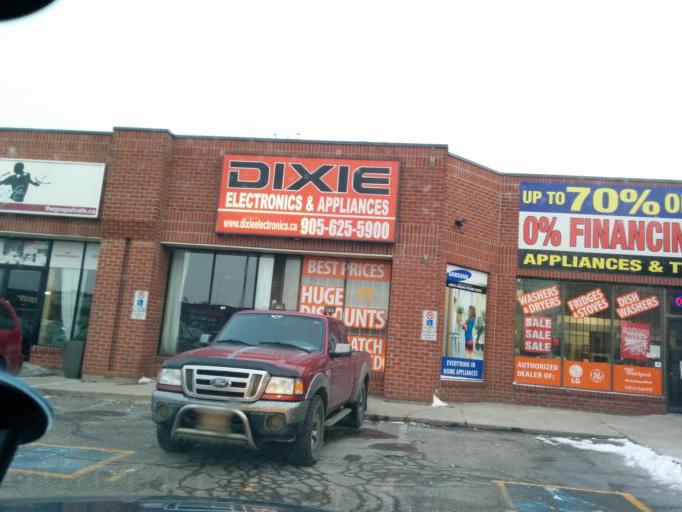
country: CA
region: Ontario
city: Etobicoke
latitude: 43.6362
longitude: -79.6238
